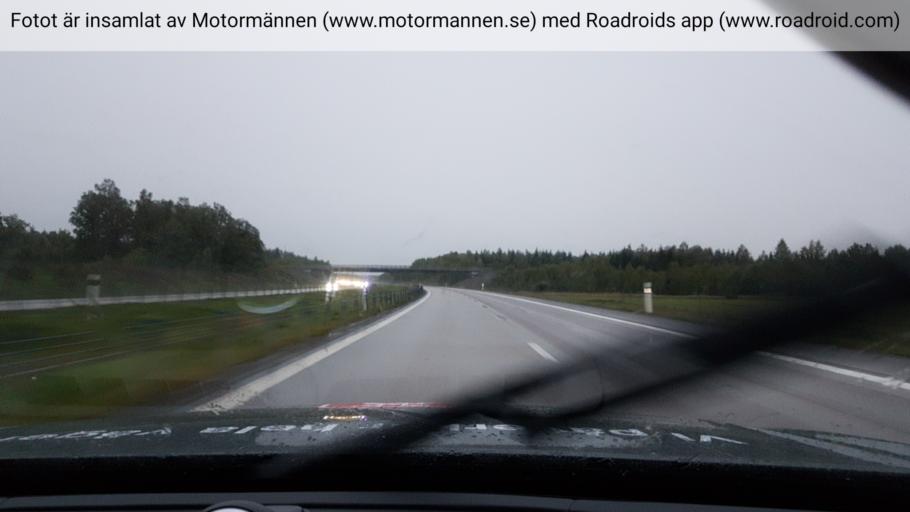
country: SE
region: Uppsala
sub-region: Osthammars Kommun
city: Bjorklinge
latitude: 60.0569
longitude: 17.6145
